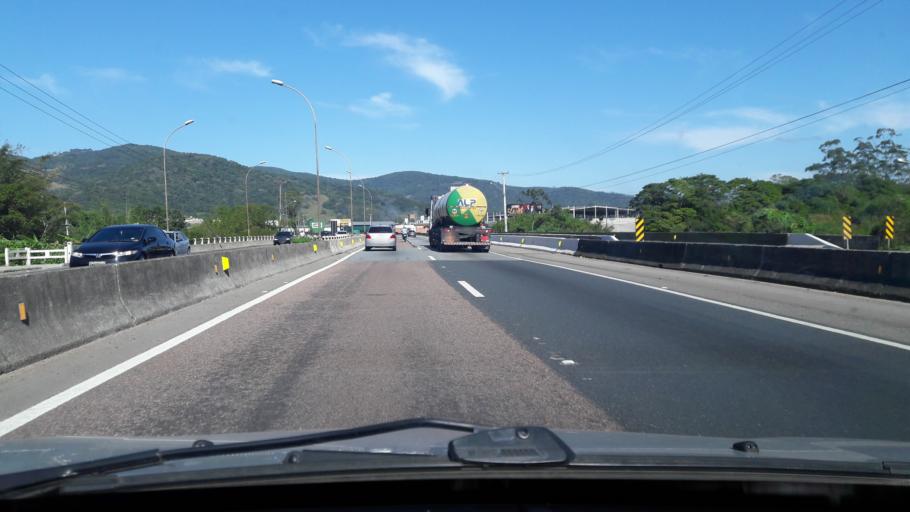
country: BR
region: Santa Catarina
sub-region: Biguacu
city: Biguacu
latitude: -27.4879
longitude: -48.6525
